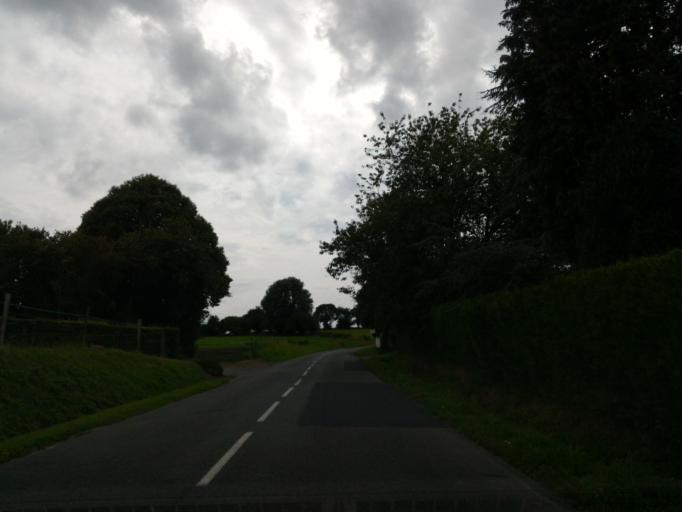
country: FR
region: Lower Normandy
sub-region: Departement de la Manche
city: La Haye-Pesnel
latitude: 48.7880
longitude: -1.4109
